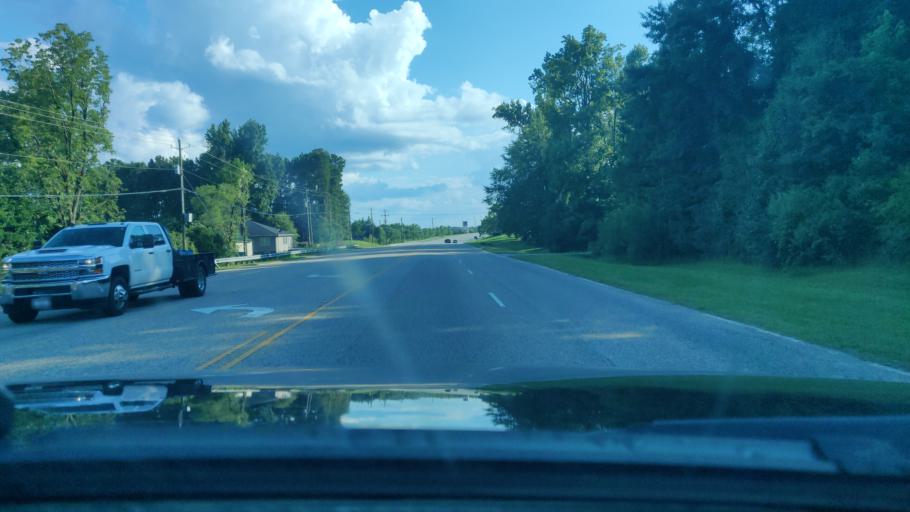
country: US
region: Alabama
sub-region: Lee County
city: Auburn
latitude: 32.6130
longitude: -85.4260
